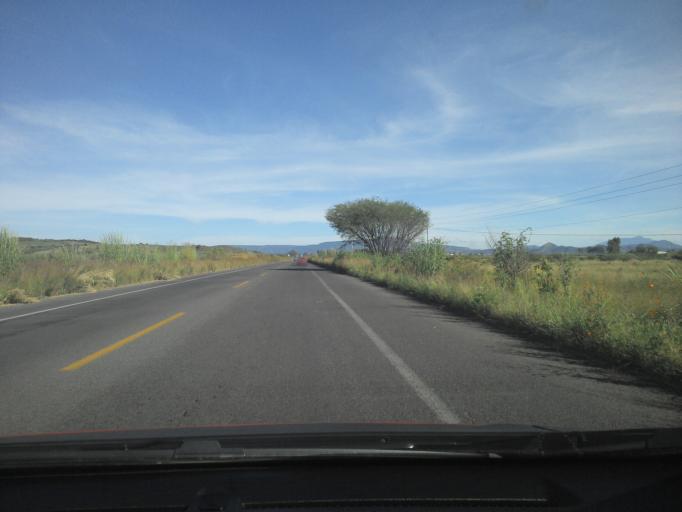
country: MX
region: Jalisco
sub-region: Teuchitlan
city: La Estanzuela
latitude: 20.6703
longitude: -103.8077
